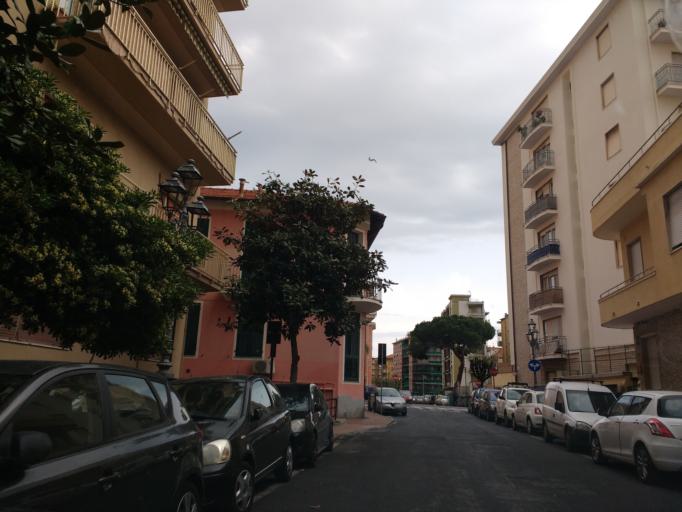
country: IT
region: Liguria
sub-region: Provincia di Imperia
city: Ventimiglia
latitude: 43.7889
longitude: 7.6109
